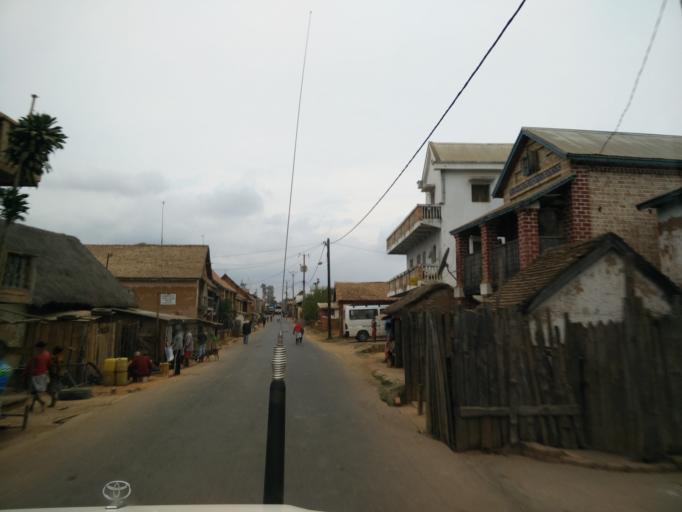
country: MG
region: Upper Matsiatra
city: Fianarantsoa
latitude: -21.5619
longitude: 47.0388
